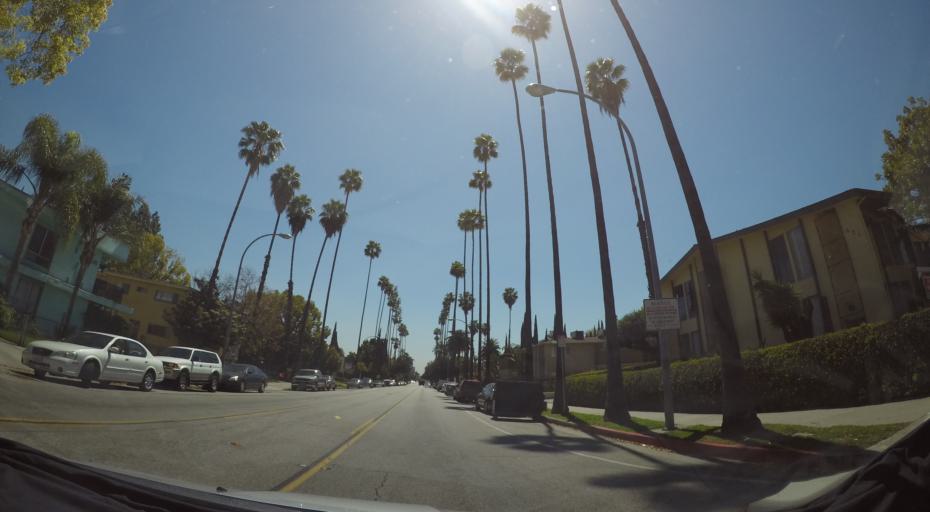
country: US
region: California
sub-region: Los Angeles County
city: Pasadena
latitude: 34.1568
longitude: -118.1415
